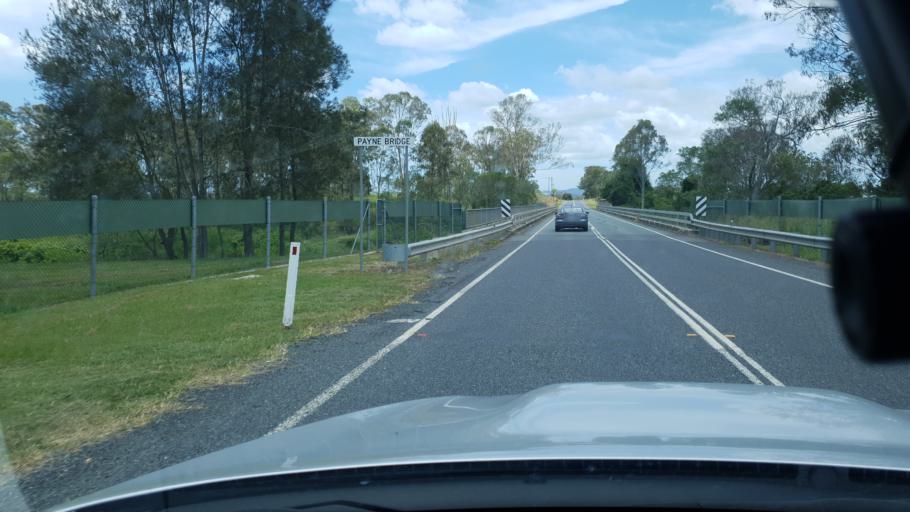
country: AU
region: Queensland
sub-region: Logan
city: North Maclean
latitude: -27.8202
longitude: 153.0034
